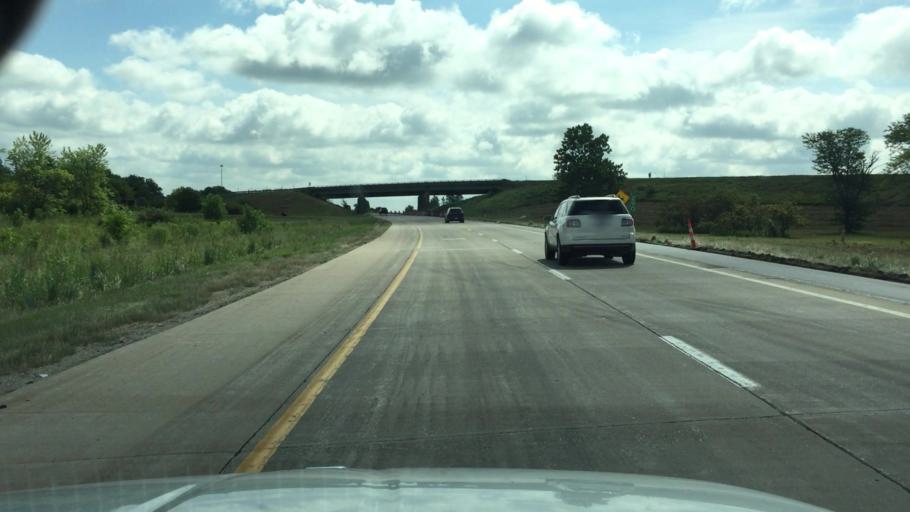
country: US
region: Iowa
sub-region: Scott County
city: Walcott
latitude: 41.6028
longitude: -90.6769
